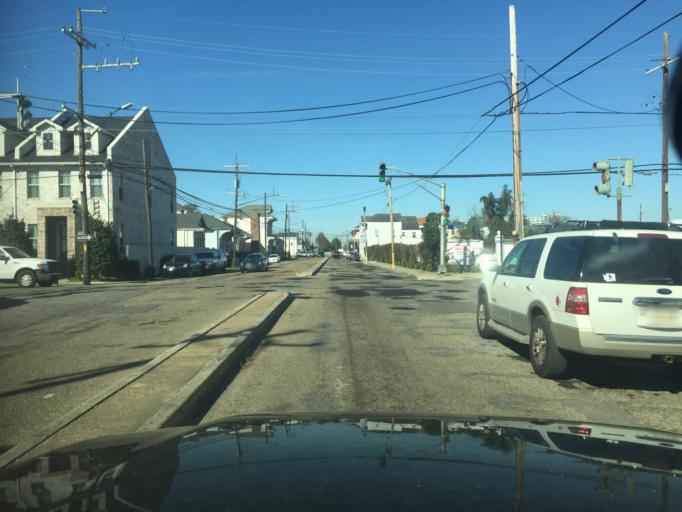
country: US
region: Louisiana
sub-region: Orleans Parish
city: New Orleans
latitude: 29.9397
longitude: -90.0765
